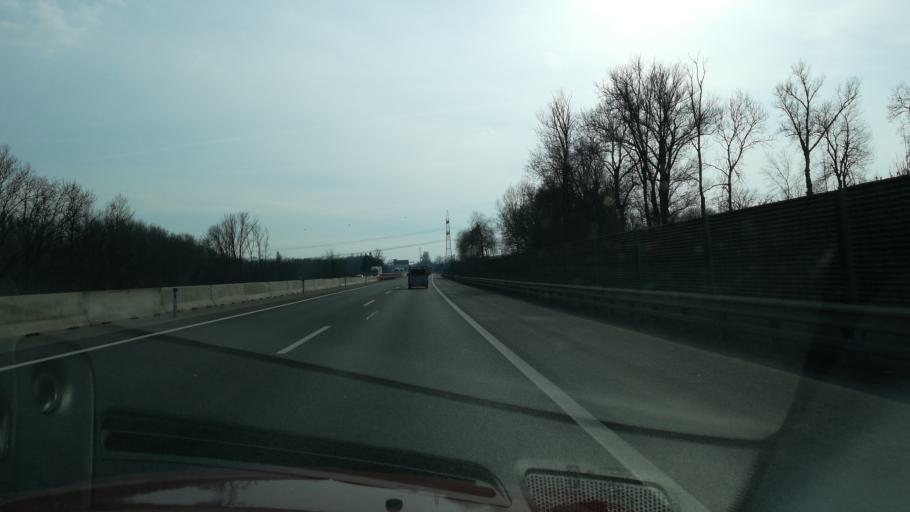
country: AT
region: Lower Austria
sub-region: Politischer Bezirk Sankt Polten
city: Traismauer
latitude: 48.3328
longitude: 15.7218
